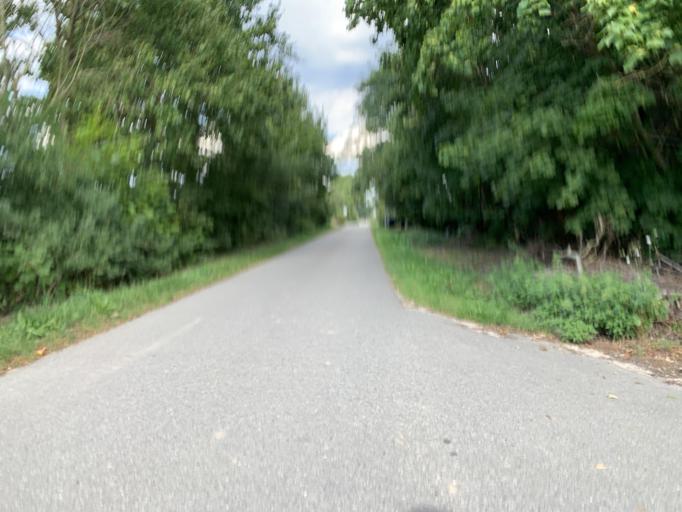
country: DE
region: Lower Saxony
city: Reinstorf
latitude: 53.2166
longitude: 10.5912
